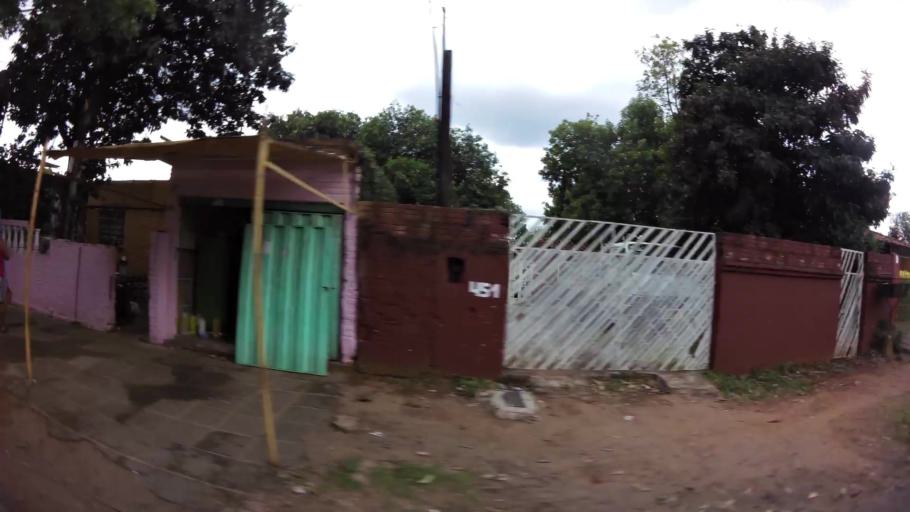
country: PY
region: Central
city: Lambare
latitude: -25.3348
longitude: -57.5666
